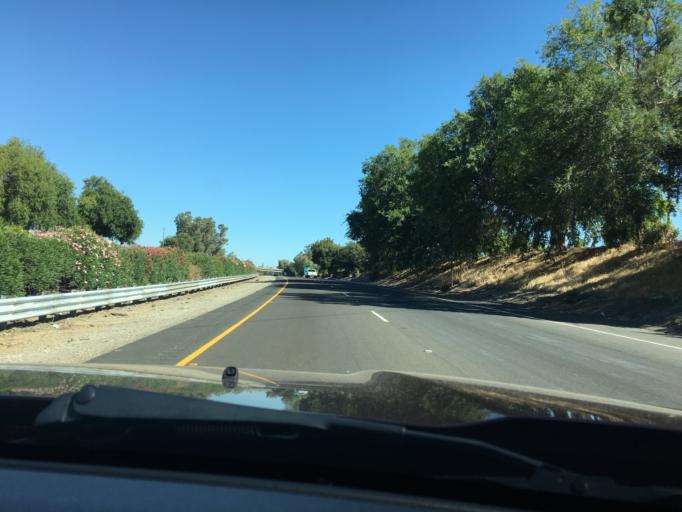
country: US
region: California
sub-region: San Joaquin County
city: Lodi
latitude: 38.1387
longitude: -121.2580
